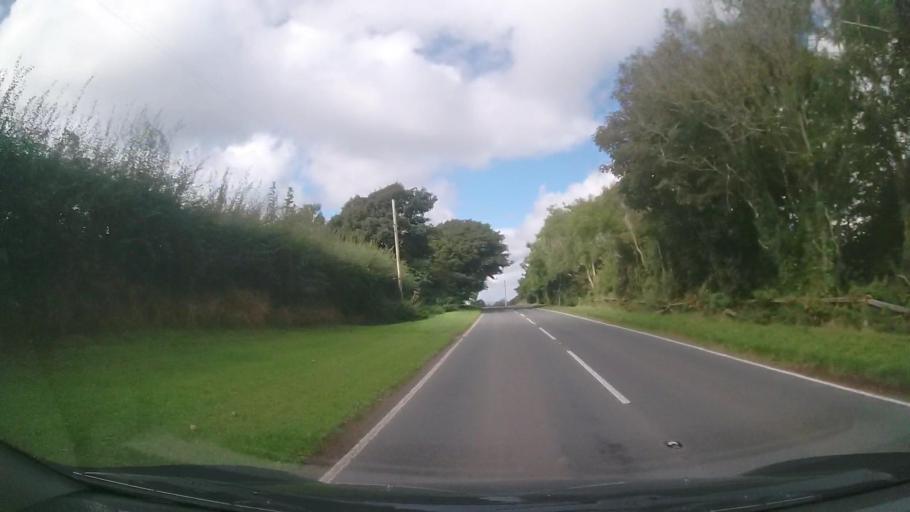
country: GB
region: Wales
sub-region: Pembrokeshire
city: Manorbier
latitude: 51.6522
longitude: -4.7874
